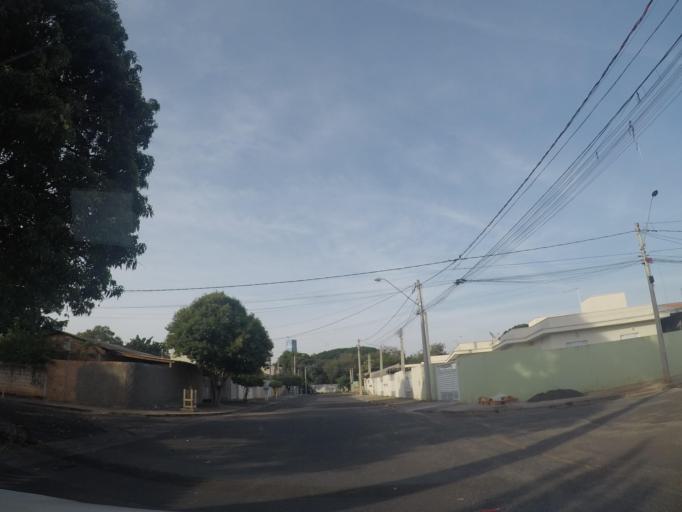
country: BR
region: Sao Paulo
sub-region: Hortolandia
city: Hortolandia
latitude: -22.8332
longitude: -47.1810
